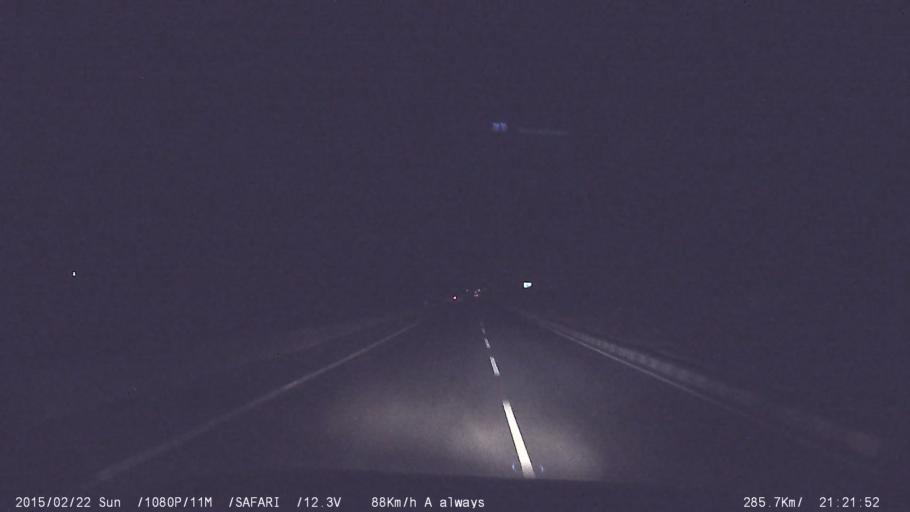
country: IN
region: Tamil Nadu
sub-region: Karur
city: Karur
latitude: 10.8682
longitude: 77.9946
